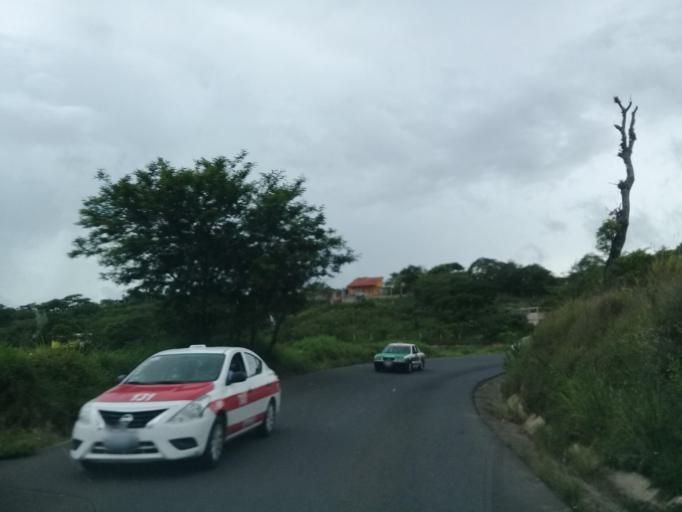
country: MX
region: Veracruz
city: El Castillo
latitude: 19.5607
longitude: -96.8510
